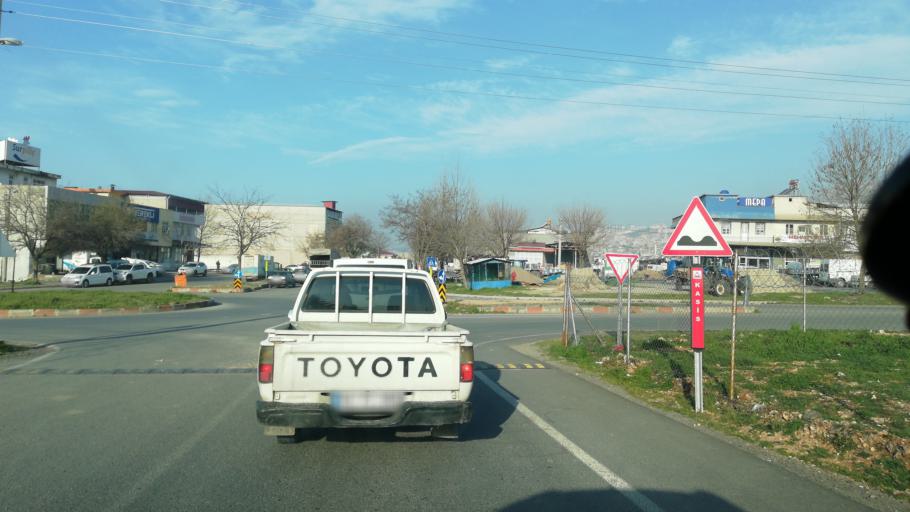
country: TR
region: Kahramanmaras
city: Kahramanmaras
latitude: 37.5638
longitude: 36.9231
